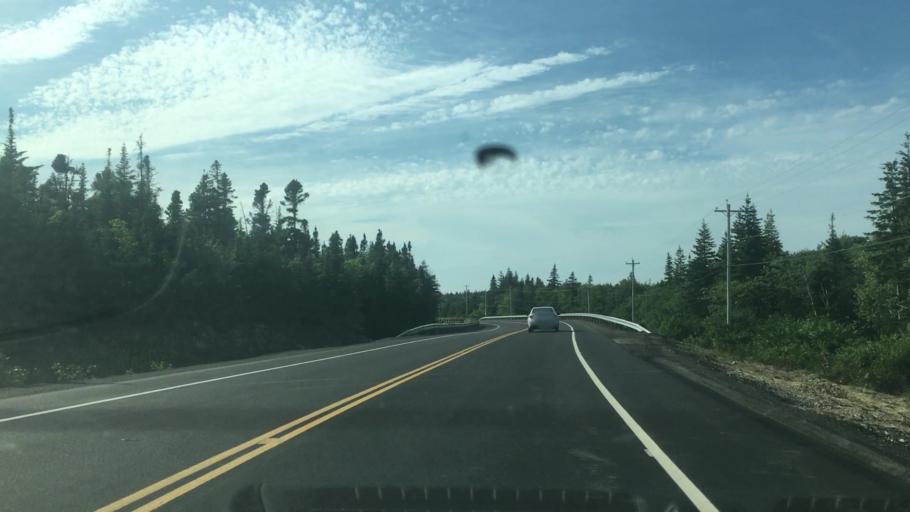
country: CA
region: Nova Scotia
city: Sydney Mines
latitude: 46.8409
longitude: -60.3918
